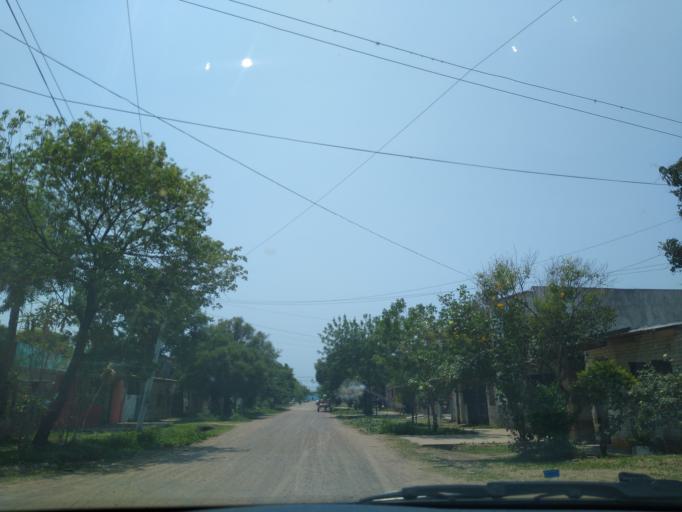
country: AR
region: Chaco
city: Barranqueras
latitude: -27.4763
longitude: -58.9324
